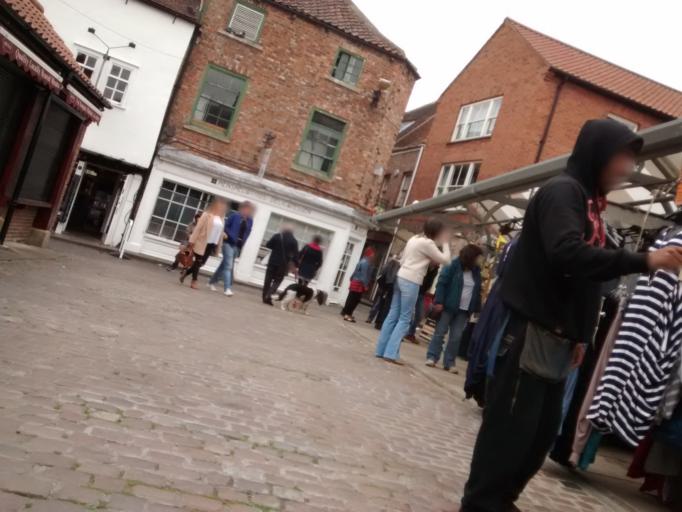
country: GB
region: England
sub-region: City of York
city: York
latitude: 53.9595
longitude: -1.0804
